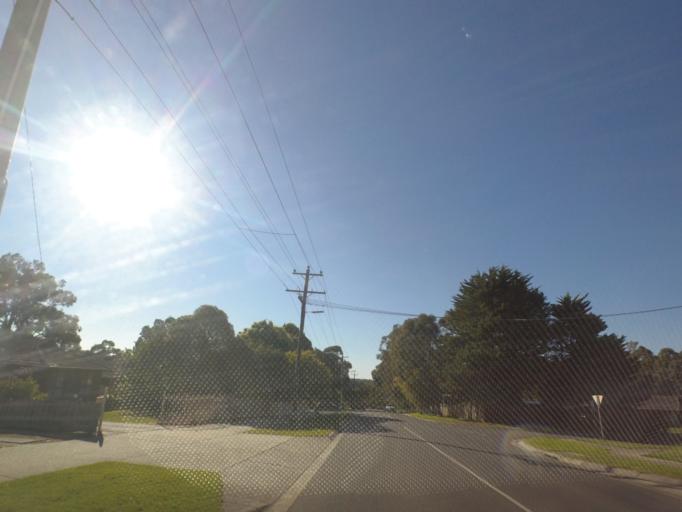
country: AU
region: Victoria
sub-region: Yarra Ranges
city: Montrose
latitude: -37.8063
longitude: 145.3395
